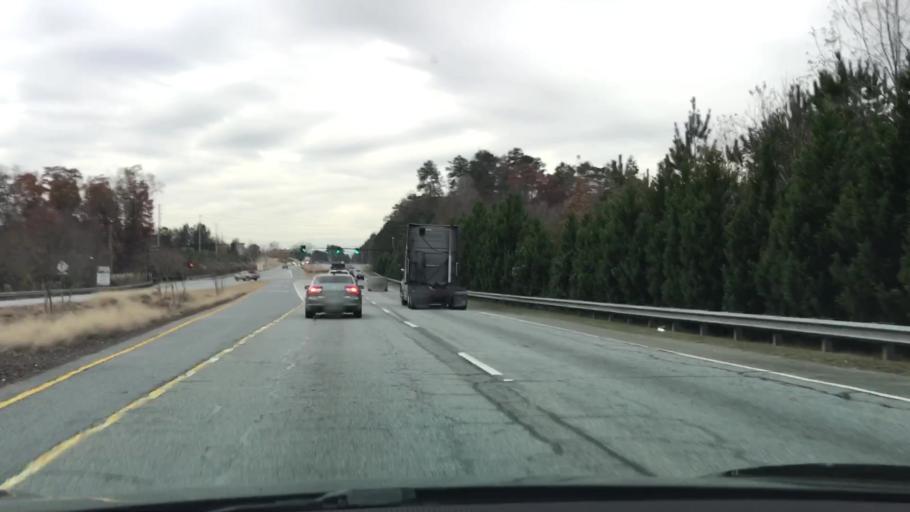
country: US
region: Georgia
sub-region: Gwinnett County
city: Suwanee
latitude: 34.0432
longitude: -84.0974
